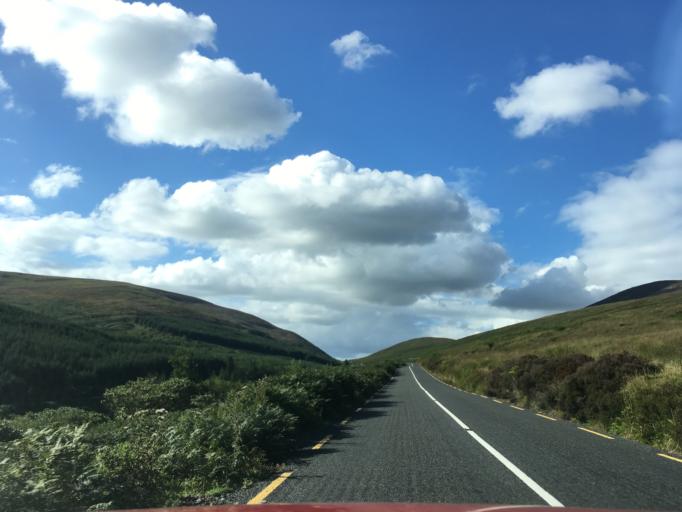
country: IE
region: Munster
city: Cahir
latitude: 52.2262
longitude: -7.9465
